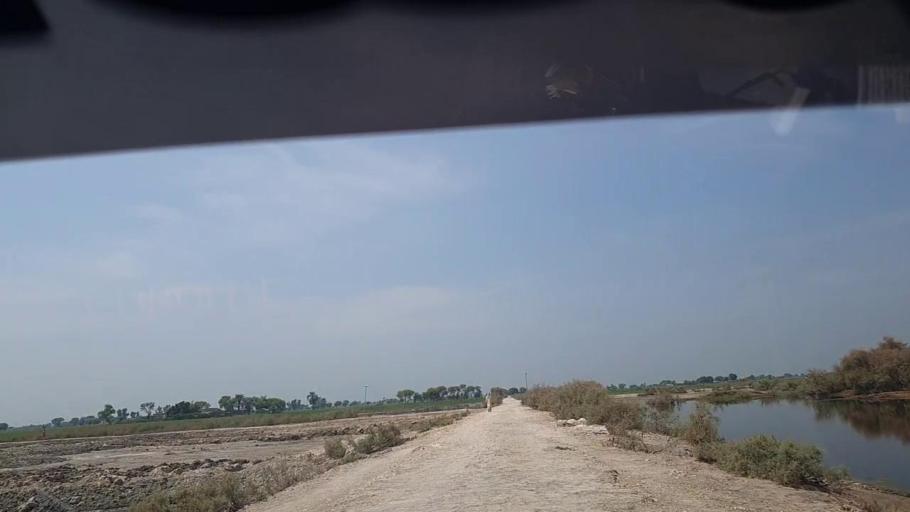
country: PK
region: Sindh
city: Thul
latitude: 28.1705
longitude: 68.7549
